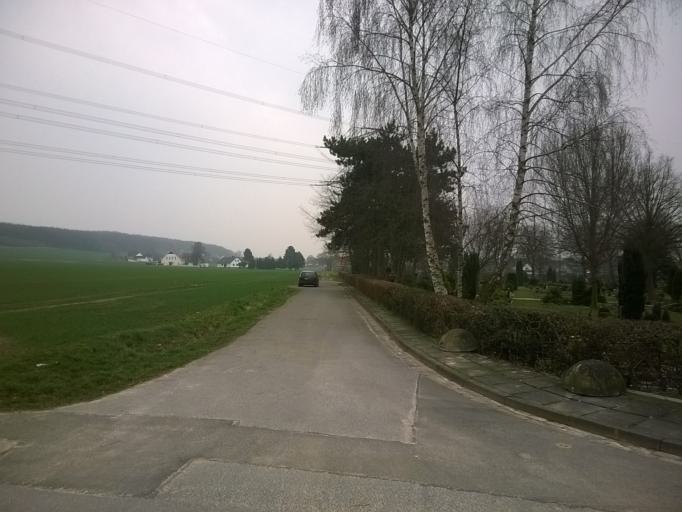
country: DE
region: North Rhine-Westphalia
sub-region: Regierungsbezirk Detmold
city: Hiddenhausen
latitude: 52.1636
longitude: 8.6385
